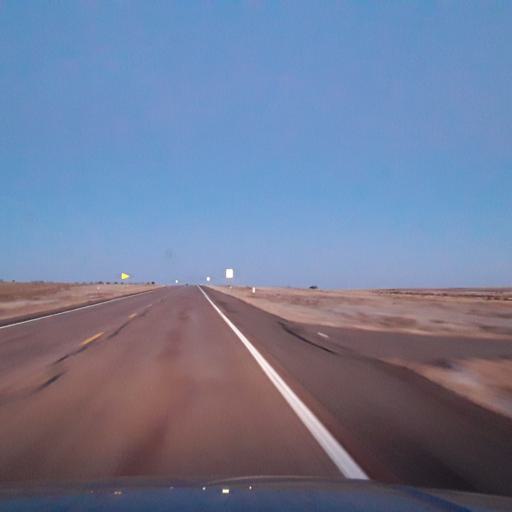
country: US
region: New Mexico
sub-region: Guadalupe County
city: Santa Rosa
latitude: 34.7674
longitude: -104.9733
